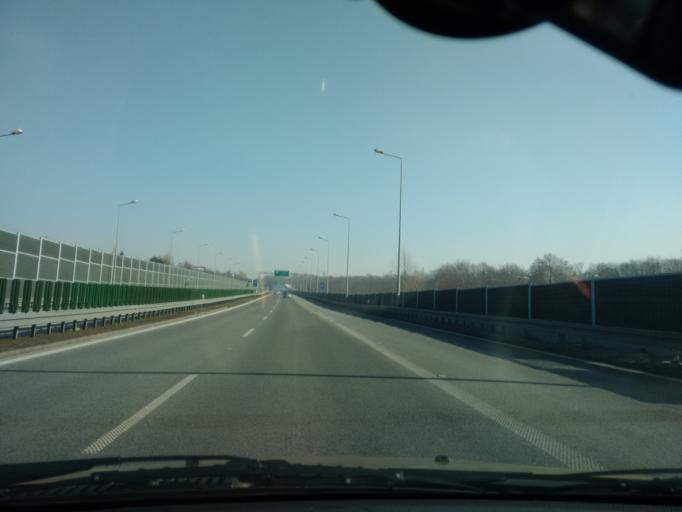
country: PL
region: Silesian Voivodeship
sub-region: Bielsko-Biala
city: Bielsko-Biala
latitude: 49.8442
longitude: 19.0713
